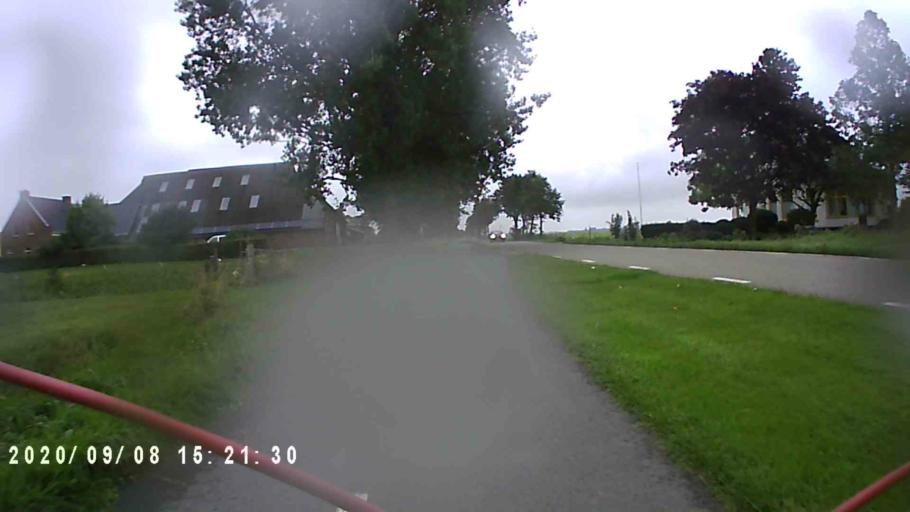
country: NL
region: Groningen
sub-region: Gemeente Bedum
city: Bedum
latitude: 53.2866
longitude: 6.6841
